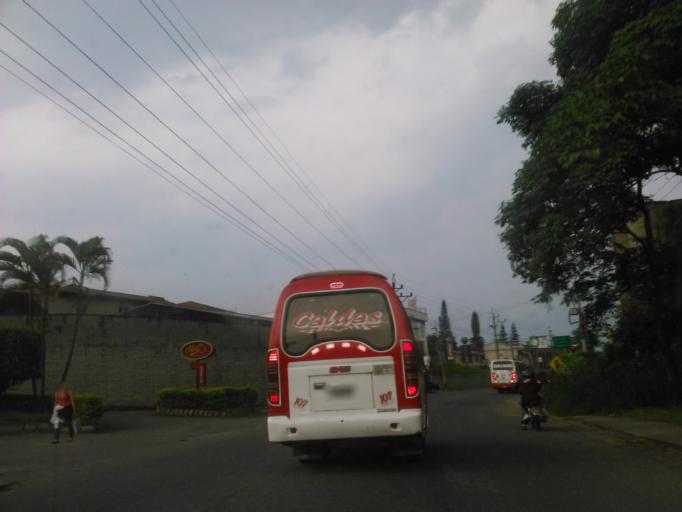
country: CO
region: Antioquia
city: La Estrella
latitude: 6.1519
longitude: -75.6347
